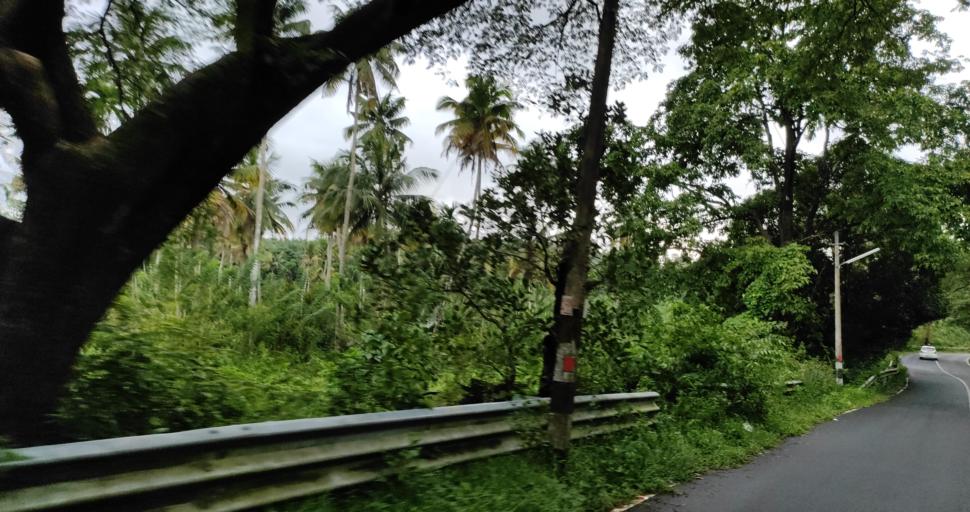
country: IN
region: Kerala
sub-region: Thrissur District
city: Kizhake Chalakudi
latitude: 10.3011
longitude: 76.4463
